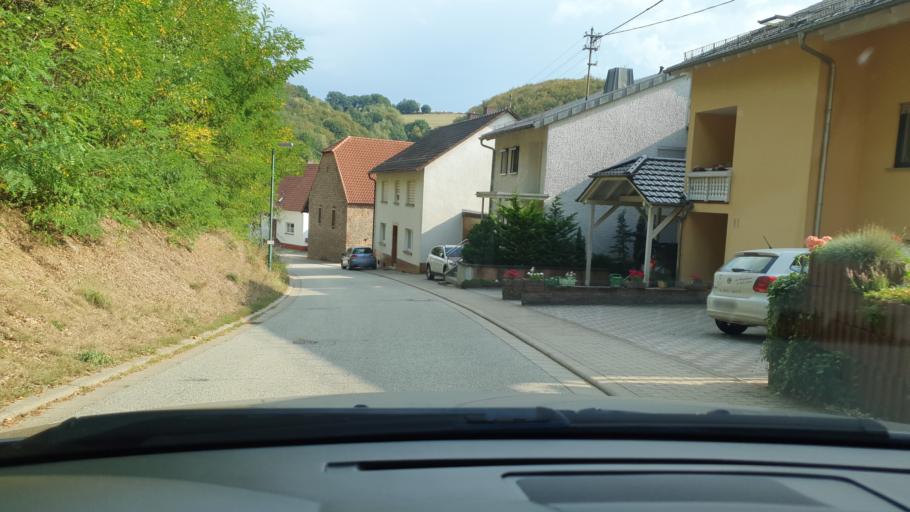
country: DE
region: Rheinland-Pfalz
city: Hettenhausen
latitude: 49.3372
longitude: 7.5538
